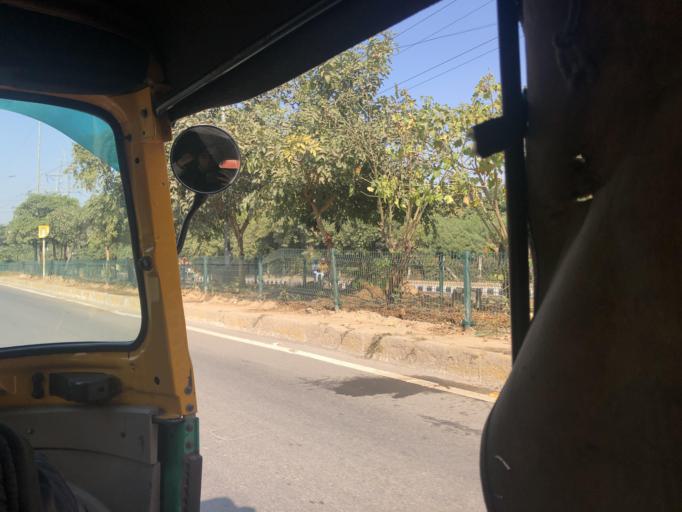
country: IN
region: Haryana
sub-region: Gurgaon
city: Gurgaon
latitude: 28.4429
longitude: 77.0842
